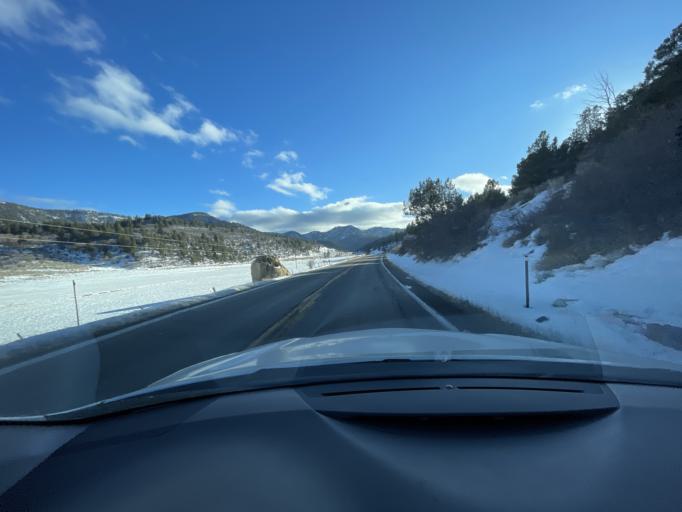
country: US
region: Colorado
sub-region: Rio Blanco County
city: Rangely
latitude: 39.6452
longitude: -108.7880
